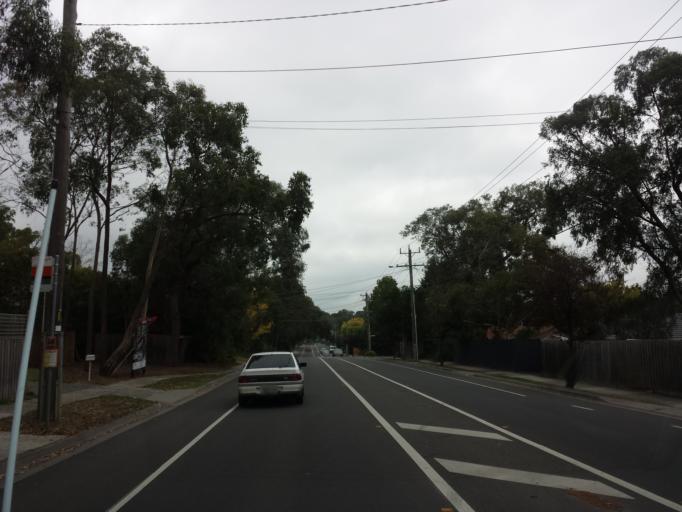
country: AU
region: Victoria
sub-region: Knox
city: The Basin
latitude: -37.8499
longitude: 145.2989
